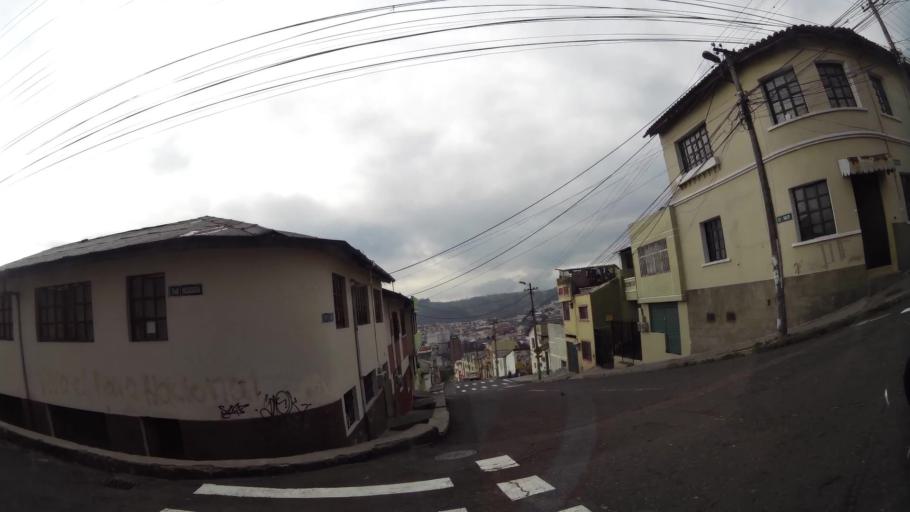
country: EC
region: Pichincha
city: Quito
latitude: -0.2109
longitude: -78.5103
